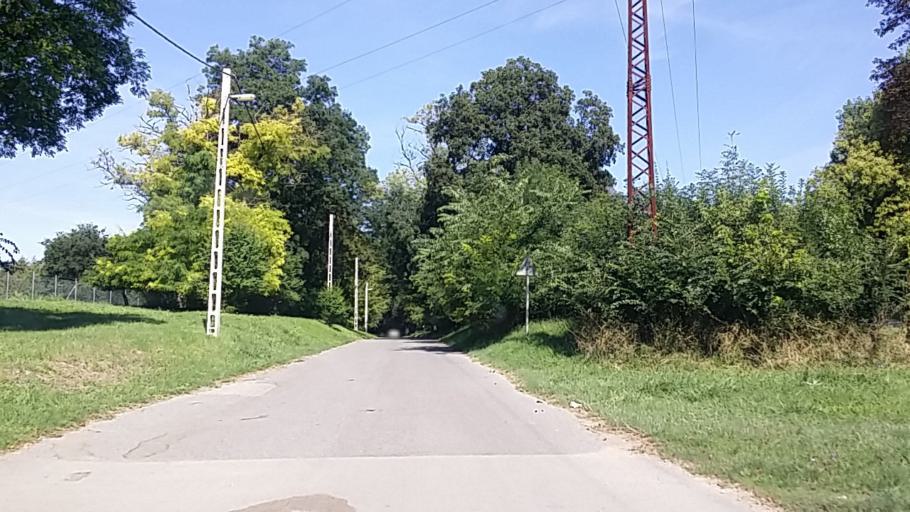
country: HU
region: Fejer
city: Deg
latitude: 46.8755
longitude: 18.4385
